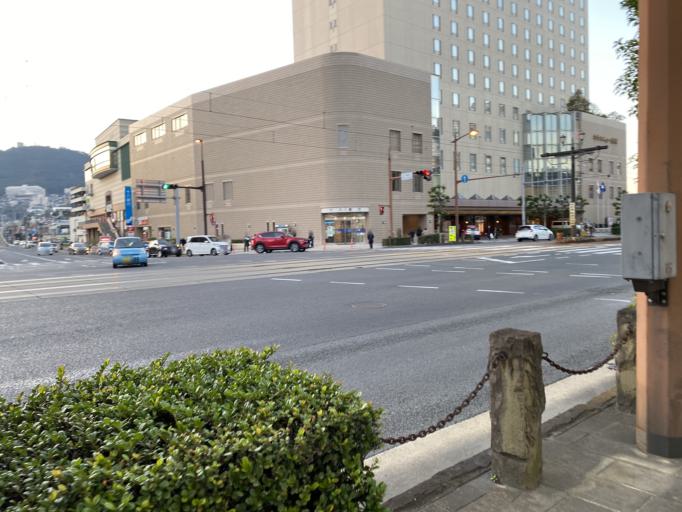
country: JP
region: Nagasaki
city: Nagasaki-shi
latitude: 32.7508
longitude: 129.8722
